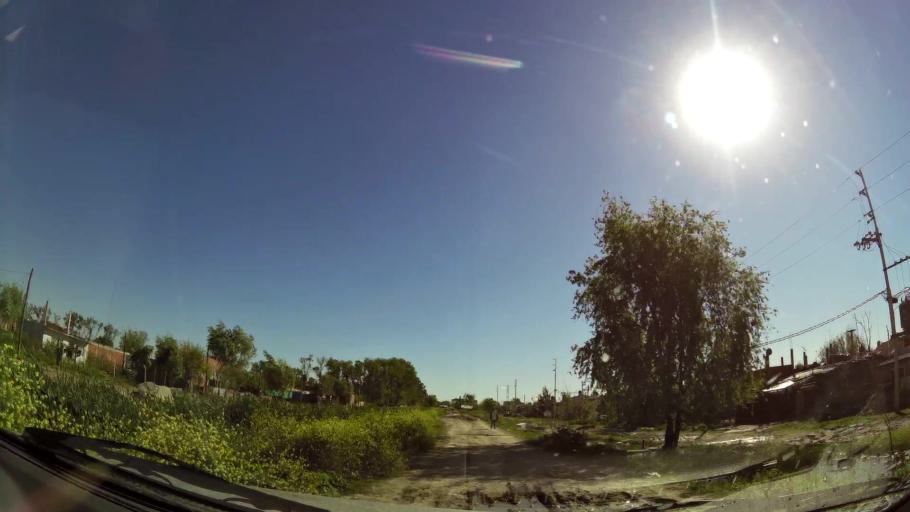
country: AR
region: Buenos Aires
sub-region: Partido de Quilmes
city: Quilmes
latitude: -34.7597
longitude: -58.3122
